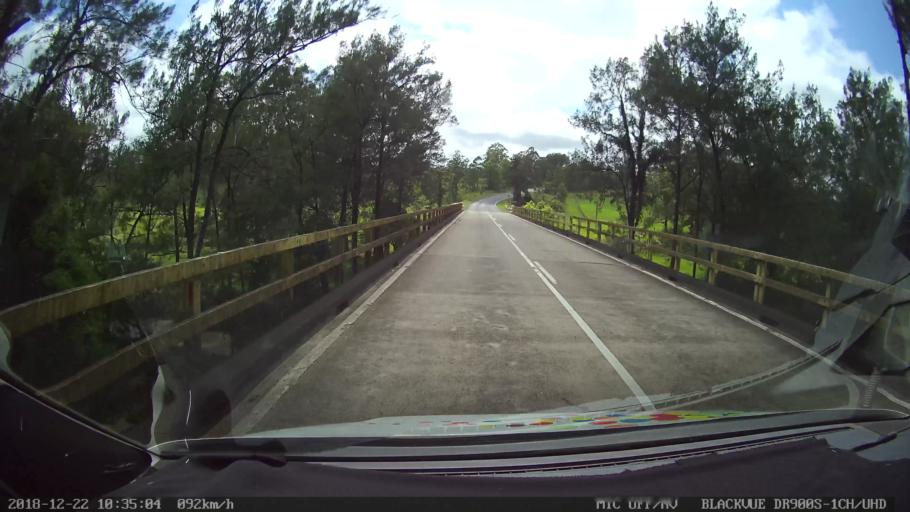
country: AU
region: New South Wales
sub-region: Clarence Valley
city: South Grafton
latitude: -29.6173
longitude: 152.6793
